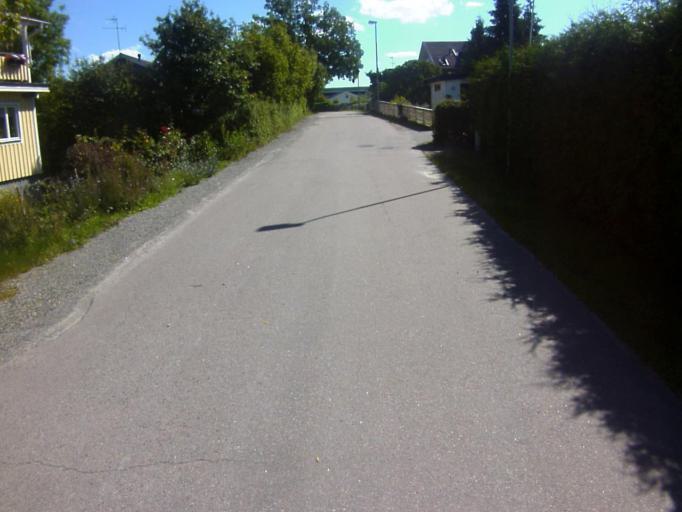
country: SE
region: Soedermanland
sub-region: Eskilstuna Kommun
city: Hallbybrunn
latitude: 59.3747
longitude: 16.4553
